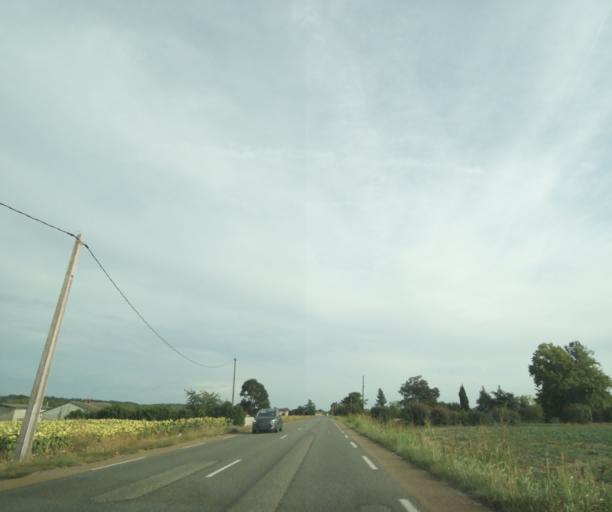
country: FR
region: Midi-Pyrenees
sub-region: Departement du Tarn-et-Garonne
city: Verdun-sur-Garonne
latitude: 43.8747
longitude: 1.2607
